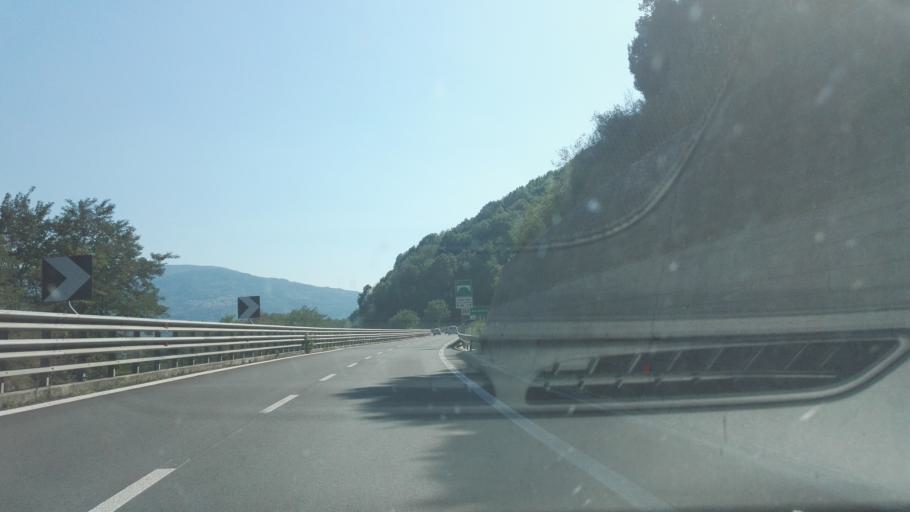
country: IT
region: Calabria
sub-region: Provincia di Cosenza
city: Altilia
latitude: 39.1346
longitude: 16.2716
